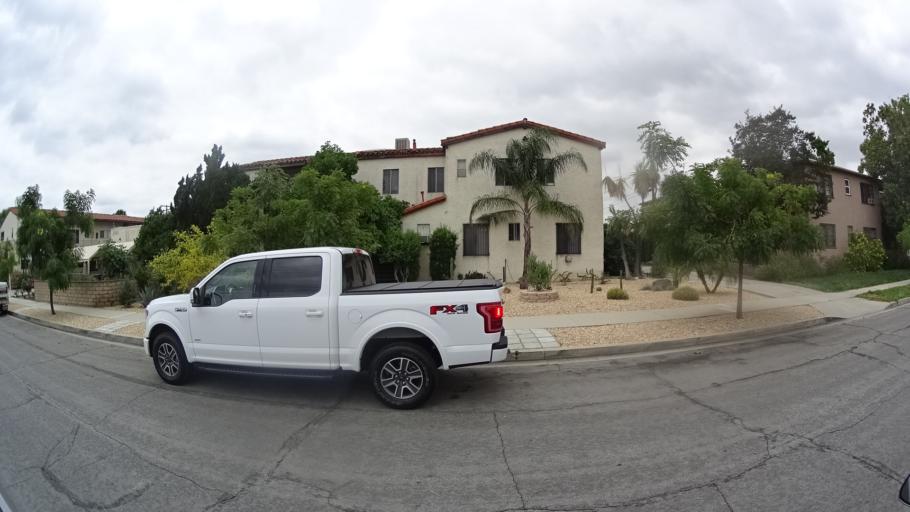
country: US
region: California
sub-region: Los Angeles County
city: Burbank
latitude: 34.1986
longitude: -118.3314
